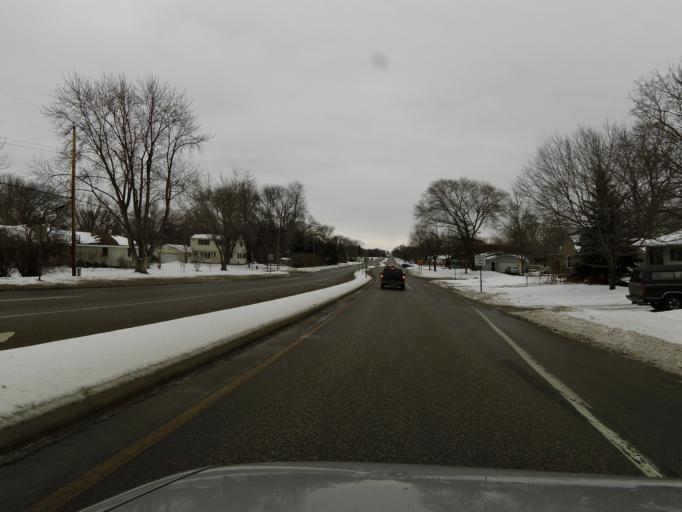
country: US
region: Minnesota
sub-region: Dakota County
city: Inver Grove Heights
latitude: 44.8480
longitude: -93.0371
